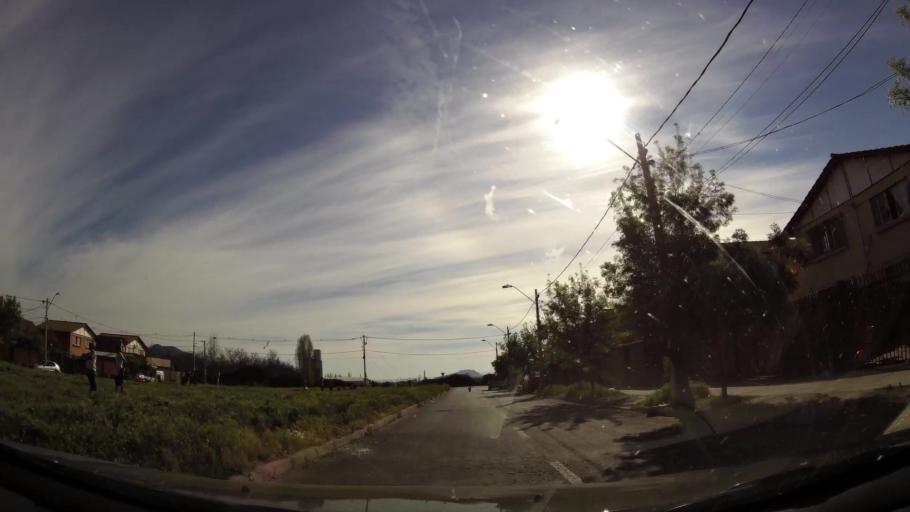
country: CL
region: Santiago Metropolitan
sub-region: Provincia de Cordillera
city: Puente Alto
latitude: -33.6313
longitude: -70.5951
